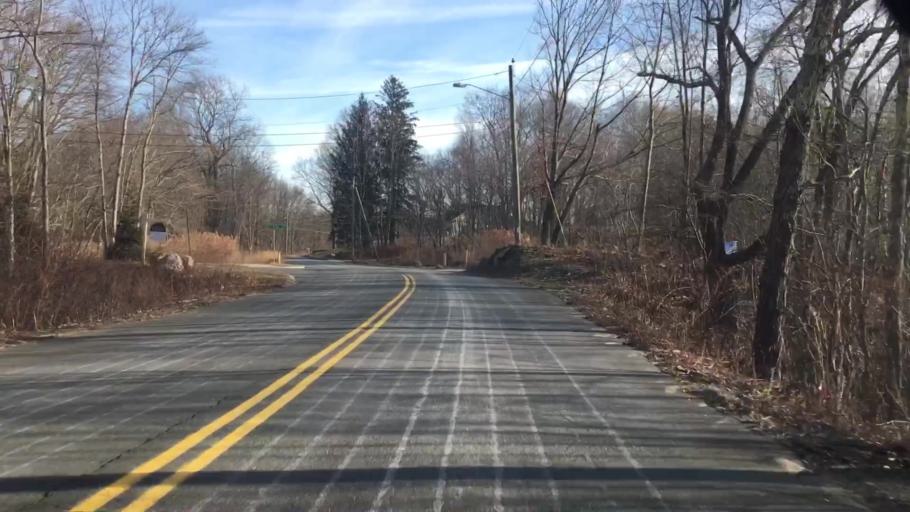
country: US
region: Connecticut
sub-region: New Haven County
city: Prospect
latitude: 41.5331
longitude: -72.9652
